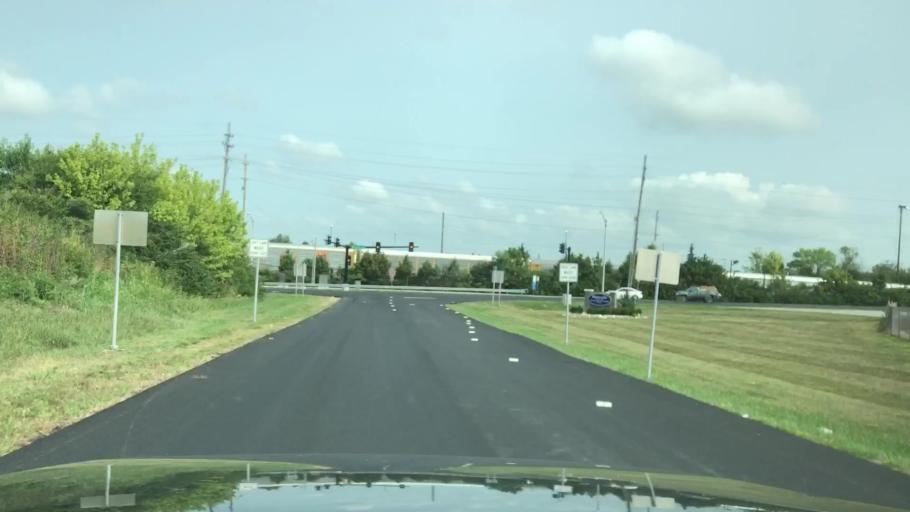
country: US
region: Missouri
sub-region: Saint Charles County
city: Wentzville
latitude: 38.8117
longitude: -90.8408
